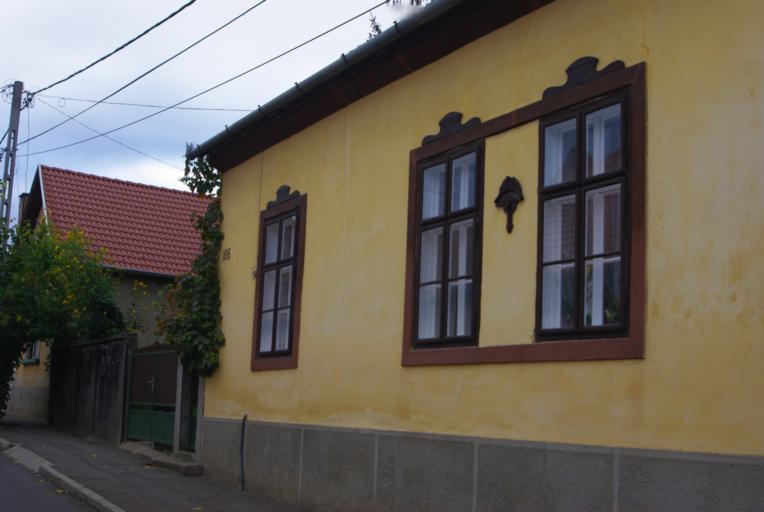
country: HU
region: Pest
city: Nagymaros
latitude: 47.7969
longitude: 18.9595
